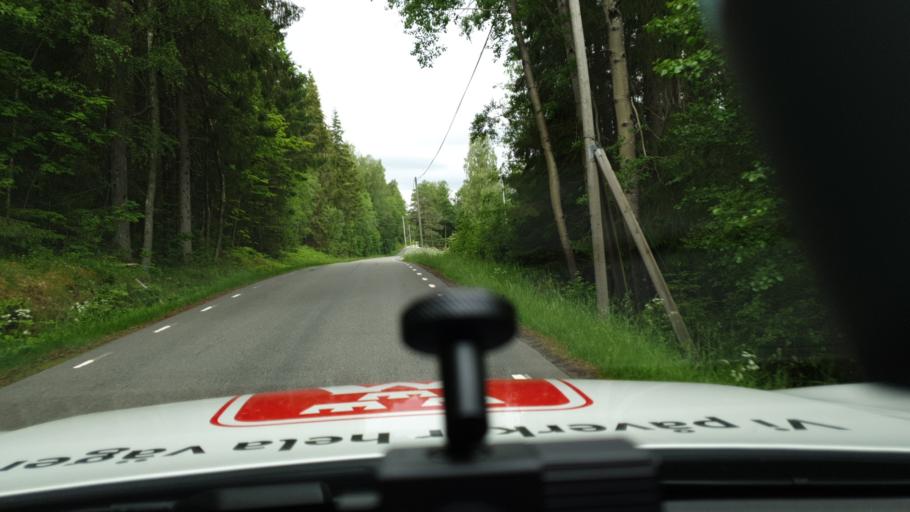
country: SE
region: Vaestra Goetaland
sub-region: Karlsborgs Kommun
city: Molltorp
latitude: 58.6671
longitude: 14.3768
